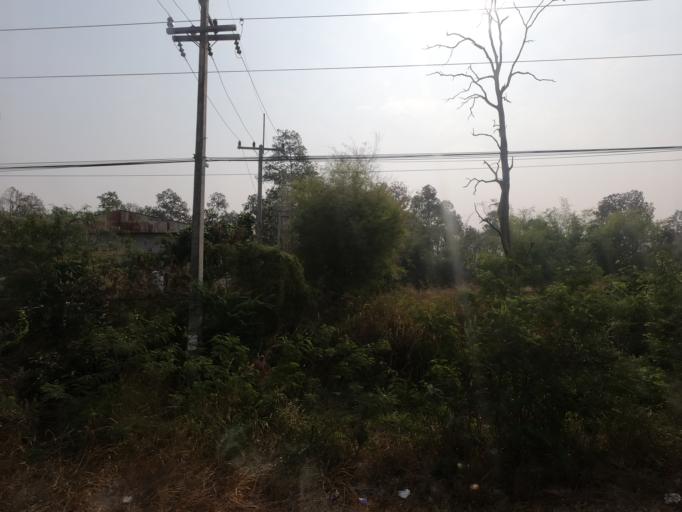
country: TH
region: Khon Kaen
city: Ban Haet
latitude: 16.1289
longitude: 102.7446
